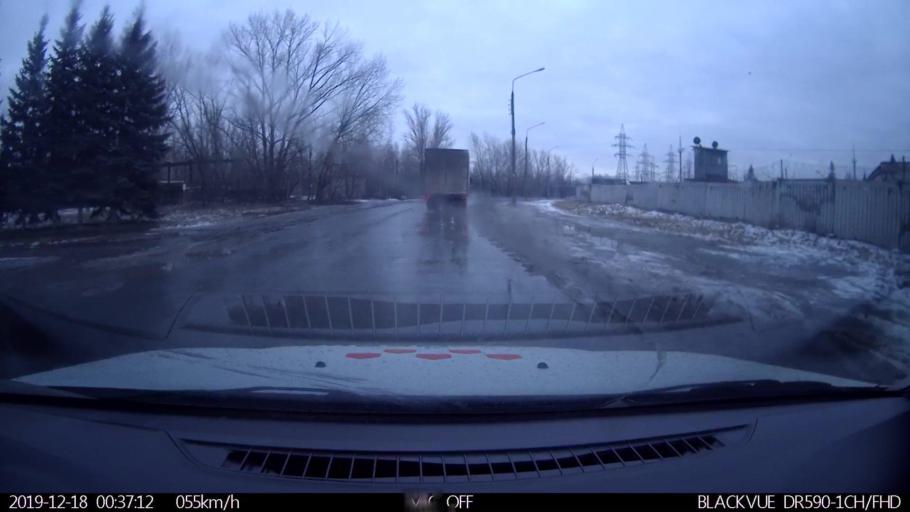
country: RU
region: Nizjnij Novgorod
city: Neklyudovo
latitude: 56.3542
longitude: 43.8951
